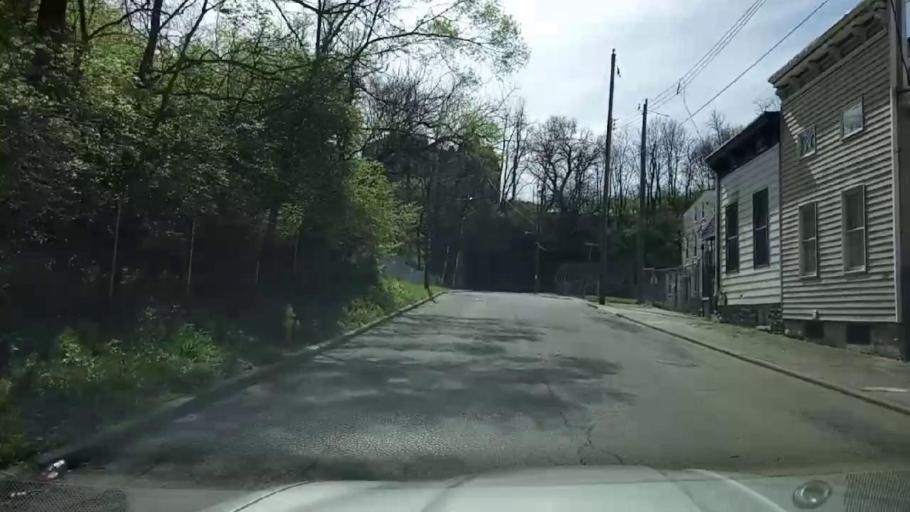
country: US
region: Kentucky
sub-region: Campbell County
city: Newport
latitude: 39.1201
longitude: -84.5128
